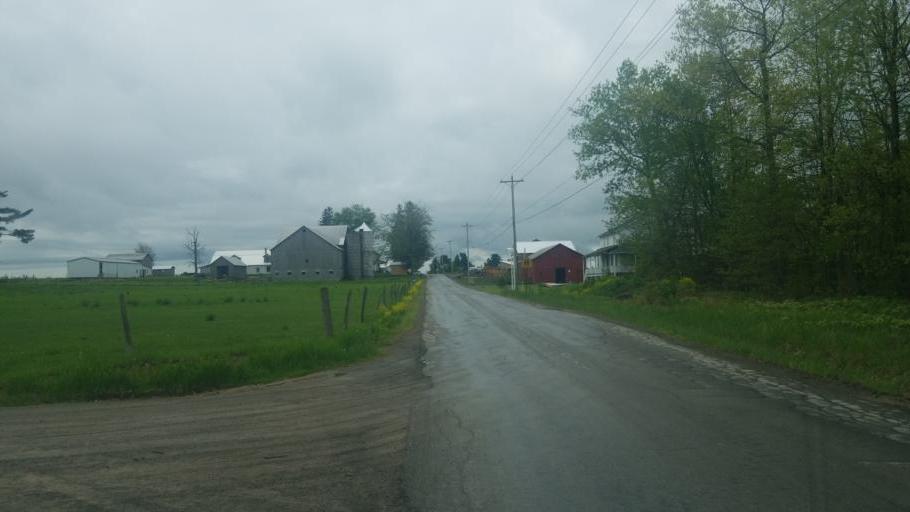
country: US
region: Pennsylvania
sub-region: Forest County
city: Tionesta
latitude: 41.4084
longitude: -79.3879
